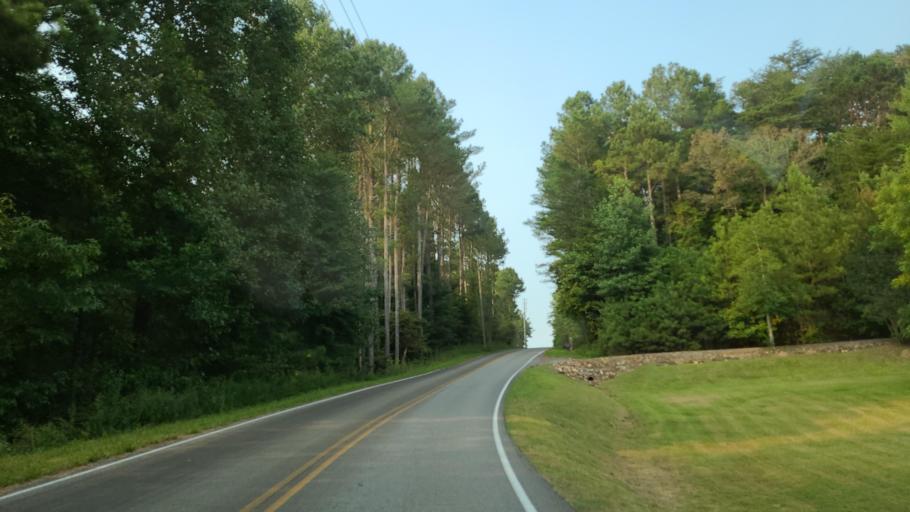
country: US
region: Georgia
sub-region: Gilmer County
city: Ellijay
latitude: 34.7858
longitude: -84.4256
